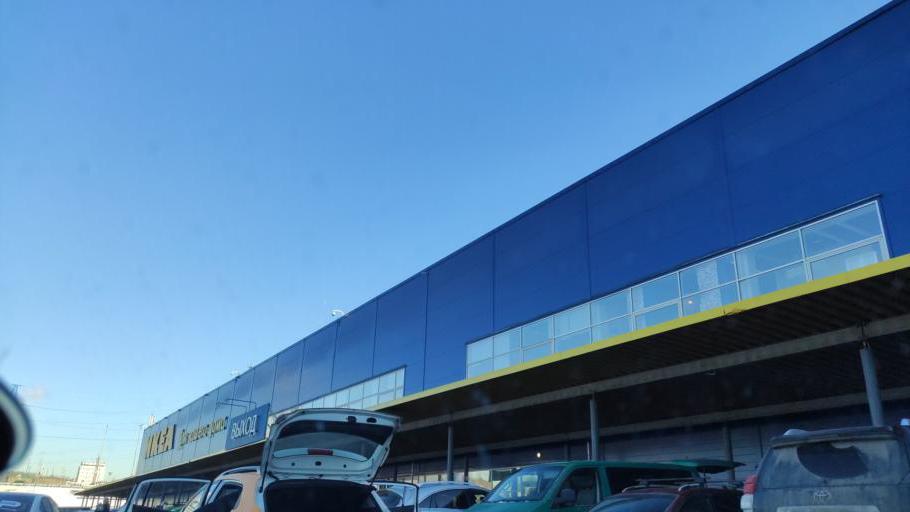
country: RU
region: Moscow
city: Tyoply Stan
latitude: 55.6038
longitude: 37.4948
